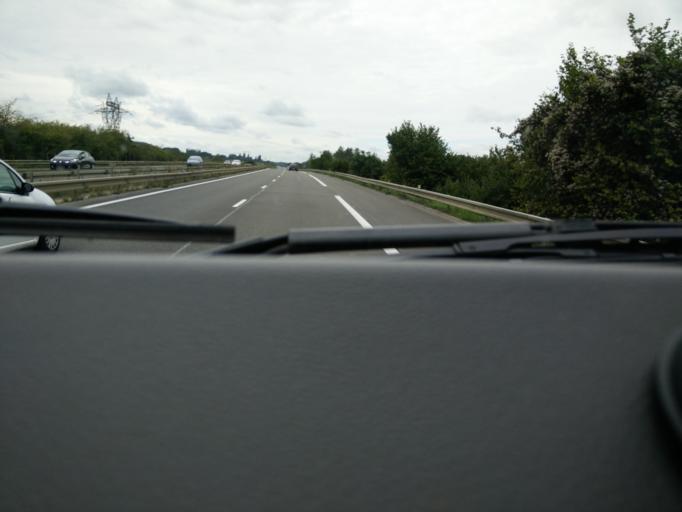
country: FR
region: Champagne-Ardenne
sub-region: Departement des Ardennes
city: Lumes
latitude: 49.7384
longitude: 4.7704
